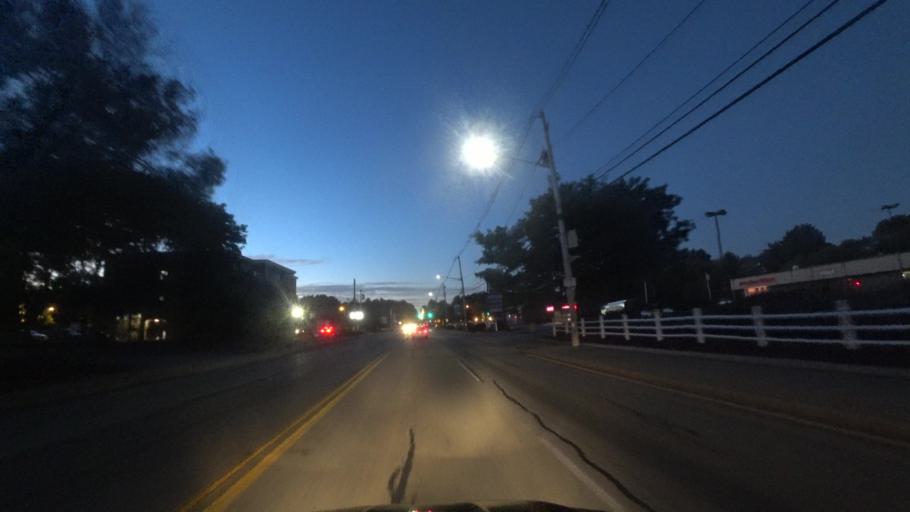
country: US
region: Massachusetts
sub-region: Middlesex County
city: North Reading
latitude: 42.5673
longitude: -71.1086
